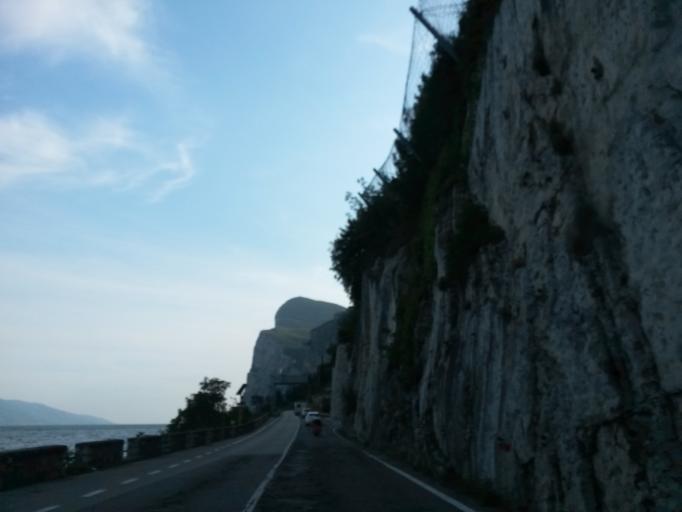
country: IT
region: Lombardy
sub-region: Provincia di Brescia
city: Pieve
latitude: 45.7692
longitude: 10.7628
